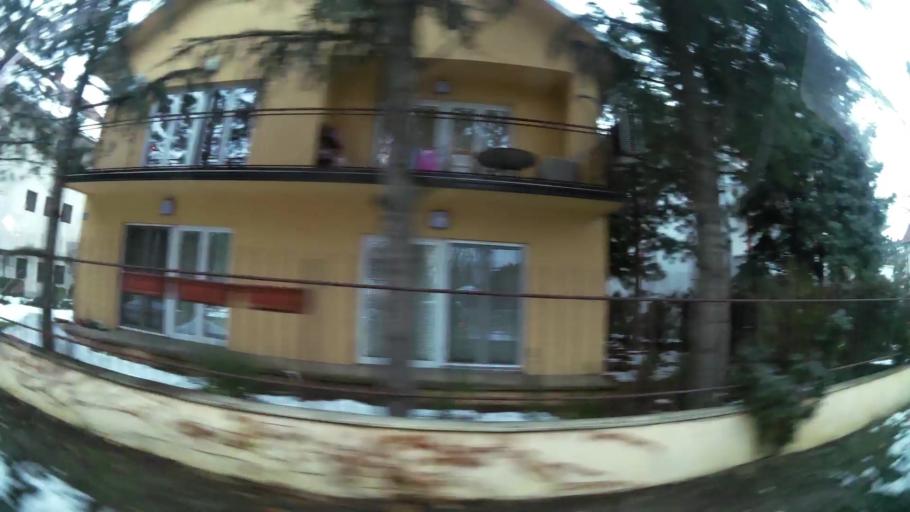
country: RS
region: Central Serbia
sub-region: Belgrade
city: Zemun
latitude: 44.8115
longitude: 20.3748
